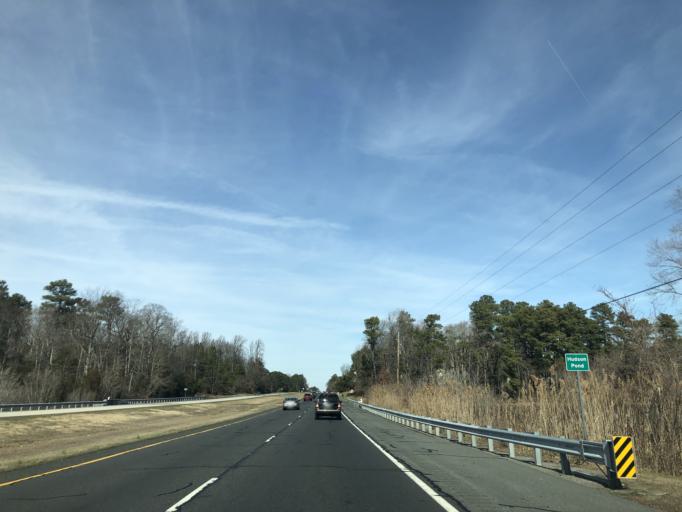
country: US
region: Delaware
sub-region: Sussex County
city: Milford
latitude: 38.8359
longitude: -75.4389
